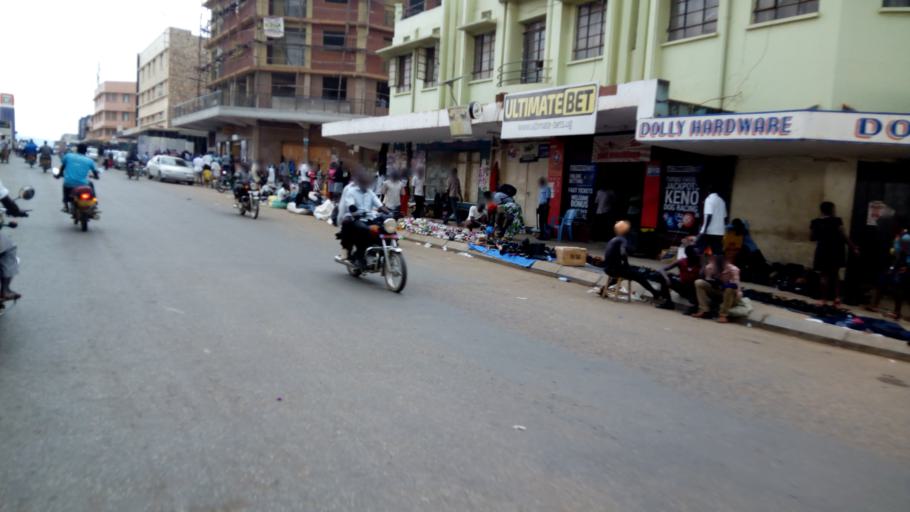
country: UG
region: Eastern Region
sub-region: Mbale District
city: Mbale
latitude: 1.0728
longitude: 34.1761
